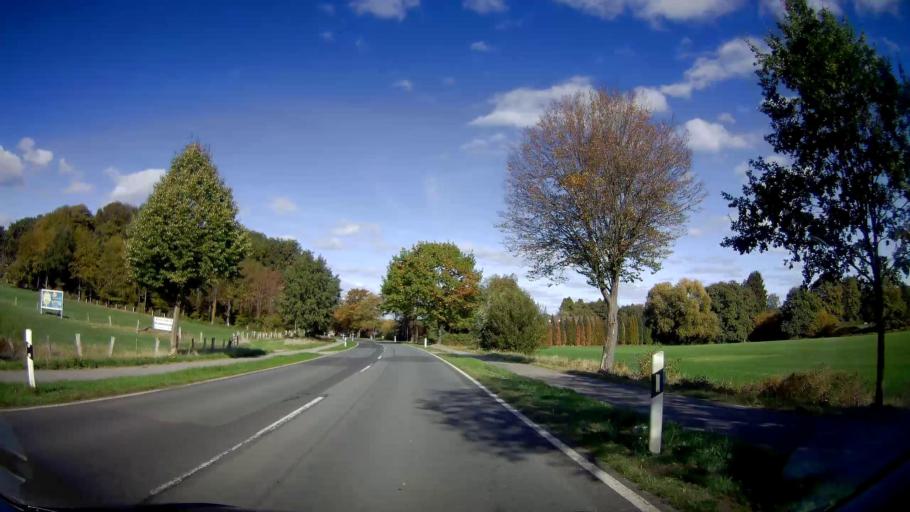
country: DE
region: North Rhine-Westphalia
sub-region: Regierungsbezirk Dusseldorf
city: Hunxe
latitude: 51.6330
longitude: 6.7622
